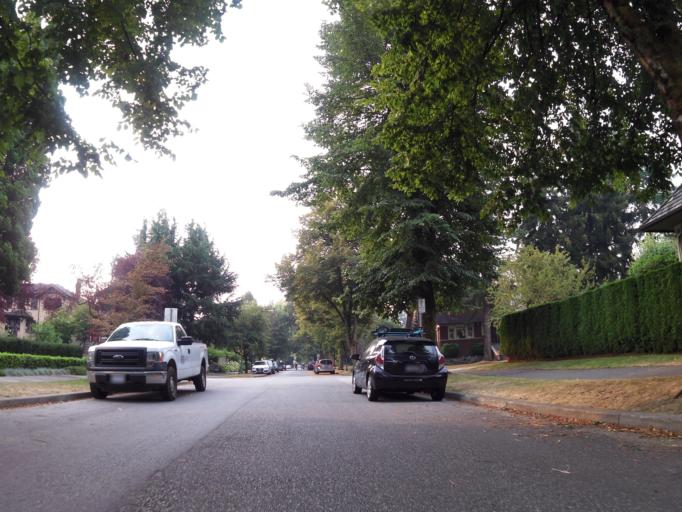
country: CA
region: British Columbia
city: West End
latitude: 49.2584
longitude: -123.1484
